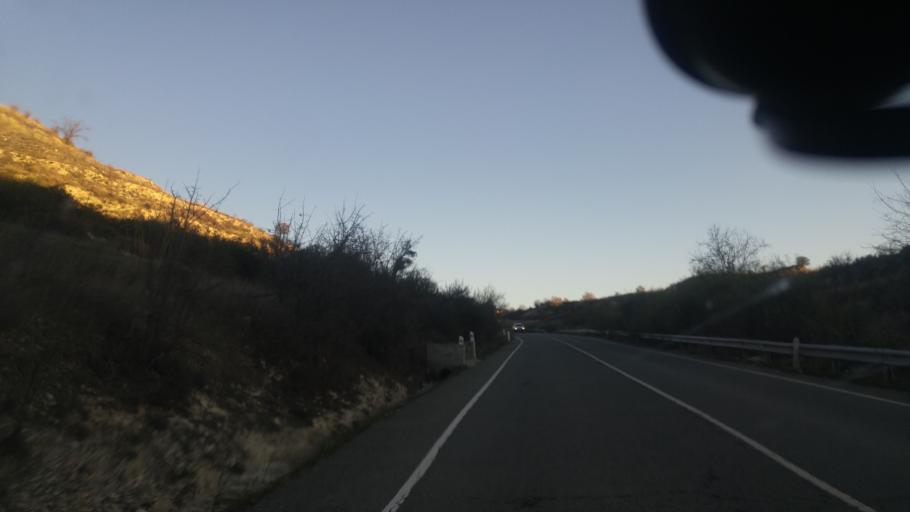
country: CY
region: Limassol
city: Pachna
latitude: 34.8003
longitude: 32.7967
